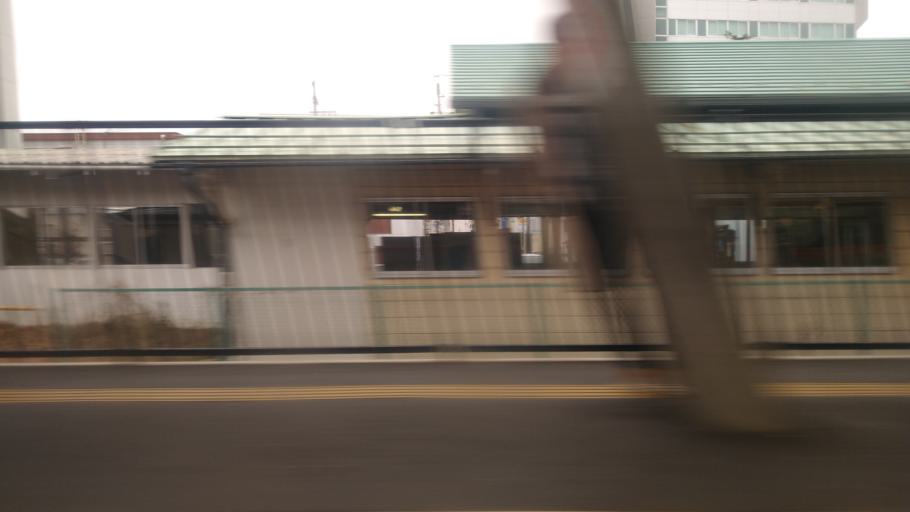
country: JP
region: Nagano
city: Matsumoto
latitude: 36.1752
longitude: 137.9565
